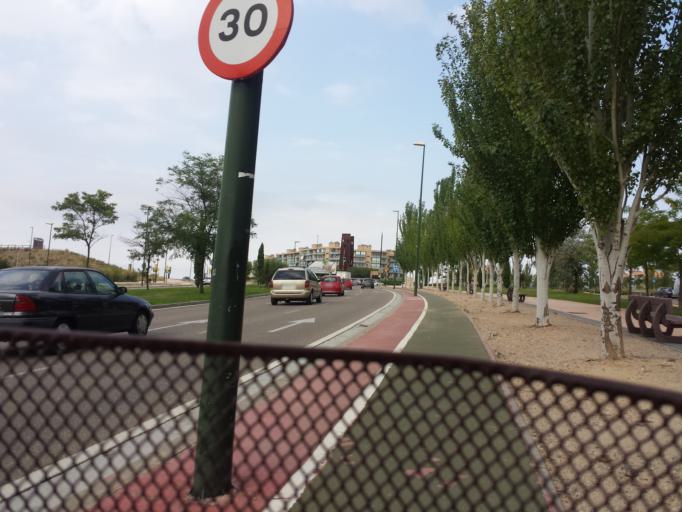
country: ES
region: Aragon
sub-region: Provincia de Zaragoza
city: Montecanal
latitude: 41.6190
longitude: -0.9247
